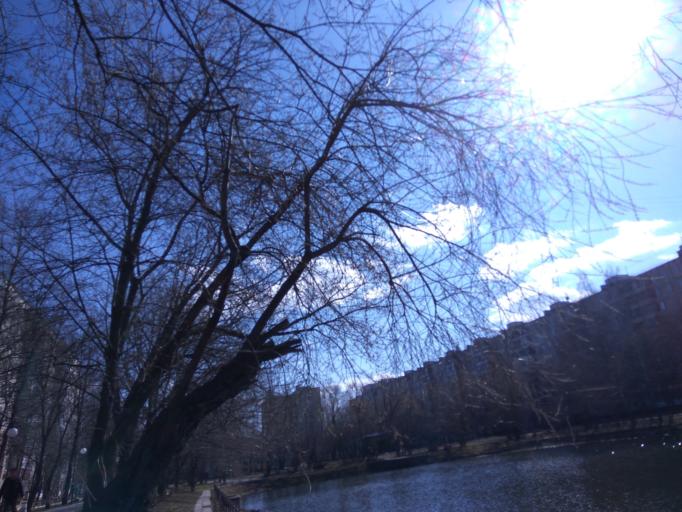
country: RU
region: Moscow
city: Ivanovskoye
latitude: 55.7716
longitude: 37.8387
